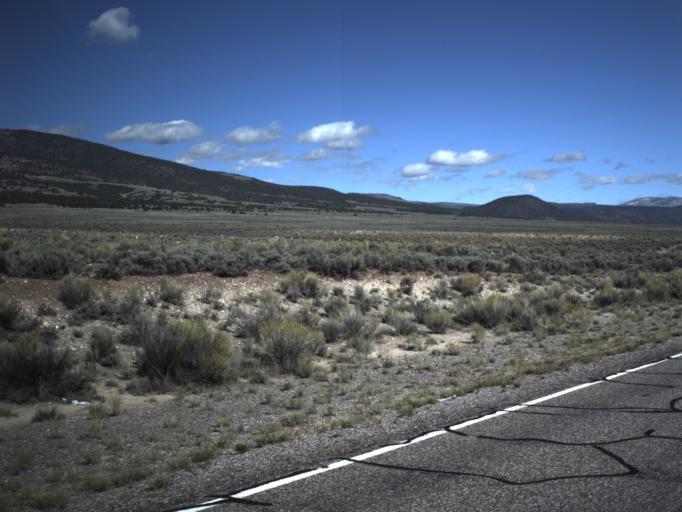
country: US
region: Utah
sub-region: Wayne County
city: Loa
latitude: 38.3647
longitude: -111.9409
